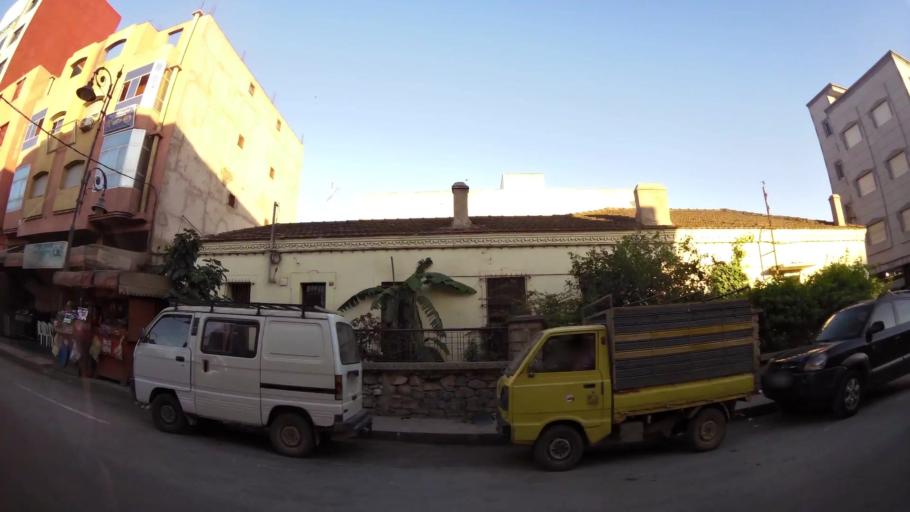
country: MA
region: Oriental
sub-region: Berkane-Taourirt
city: Berkane
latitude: 34.9239
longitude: -2.3347
